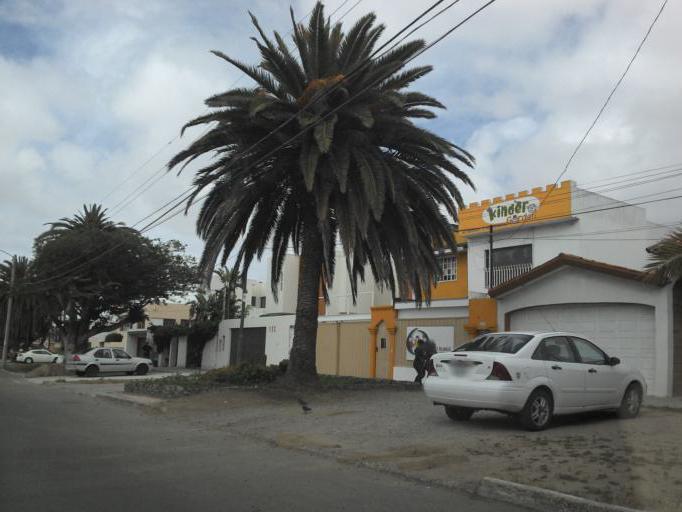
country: US
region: California
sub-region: San Diego County
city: Imperial Beach
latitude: 32.5253
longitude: -117.1161
